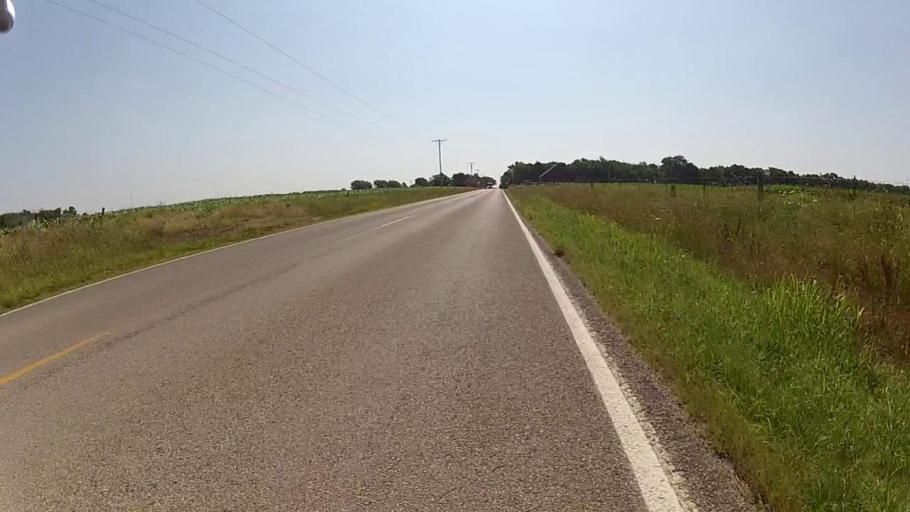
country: US
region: Kansas
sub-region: Montgomery County
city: Independence
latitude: 37.1929
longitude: -95.7453
